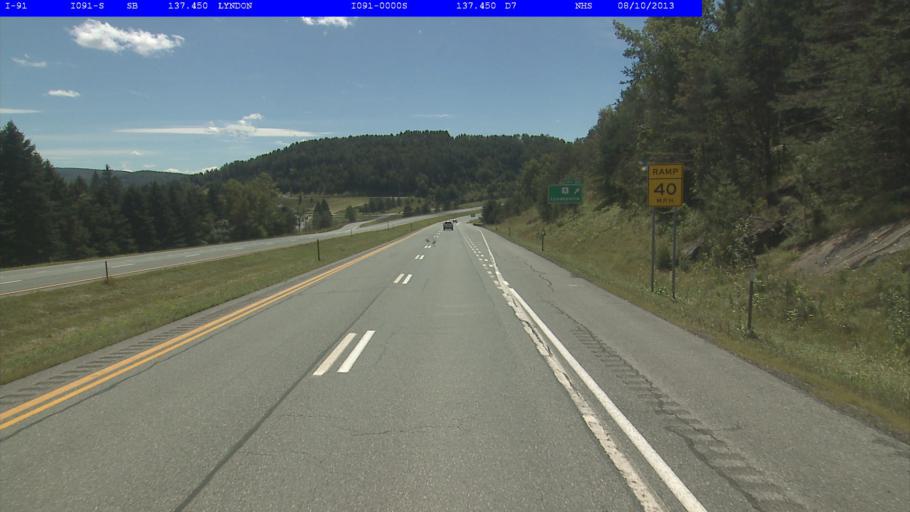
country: US
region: Vermont
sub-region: Caledonia County
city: Lyndon
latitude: 44.5212
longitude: -72.0084
